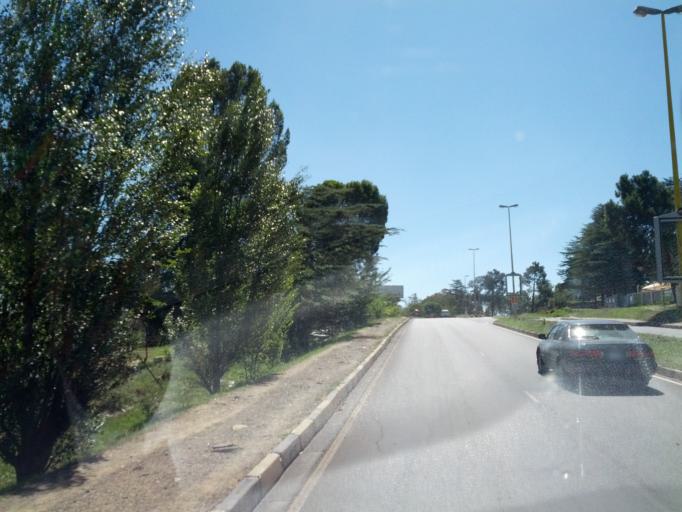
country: LS
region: Maseru
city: Maseru
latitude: -29.3079
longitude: 27.4720
